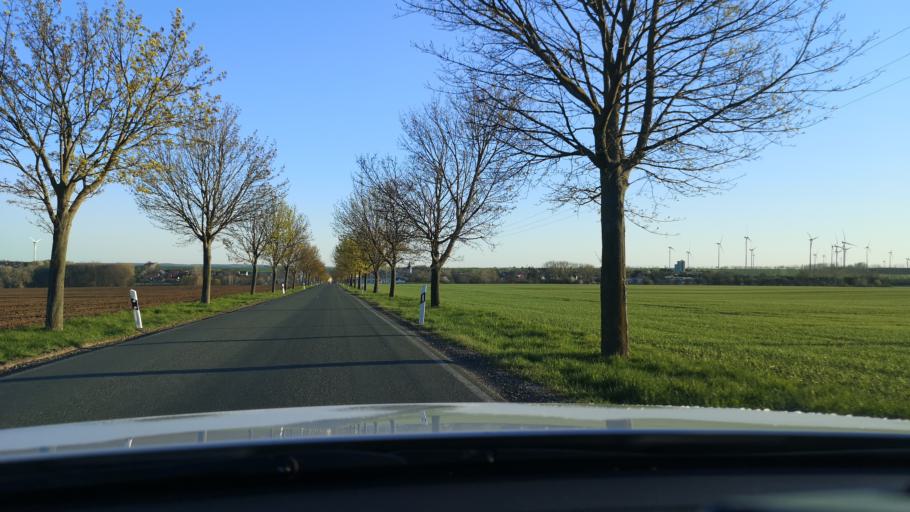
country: DE
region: Thuringia
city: Hainichen
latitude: 51.0199
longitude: 11.5995
